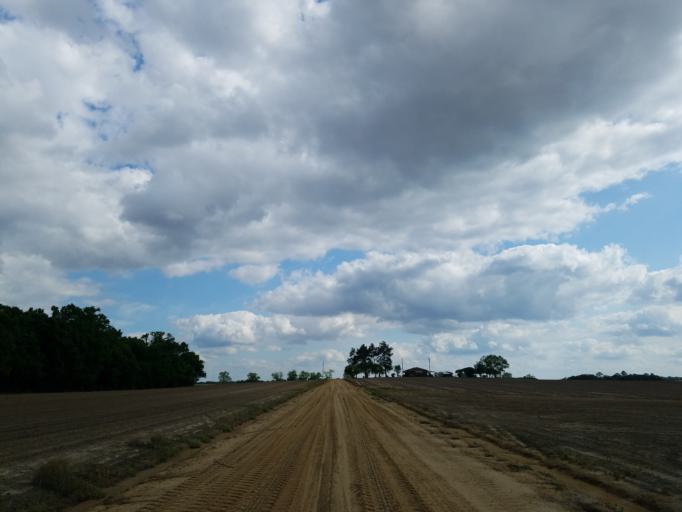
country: US
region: Georgia
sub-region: Dooly County
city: Vienna
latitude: 32.1729
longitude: -83.7759
